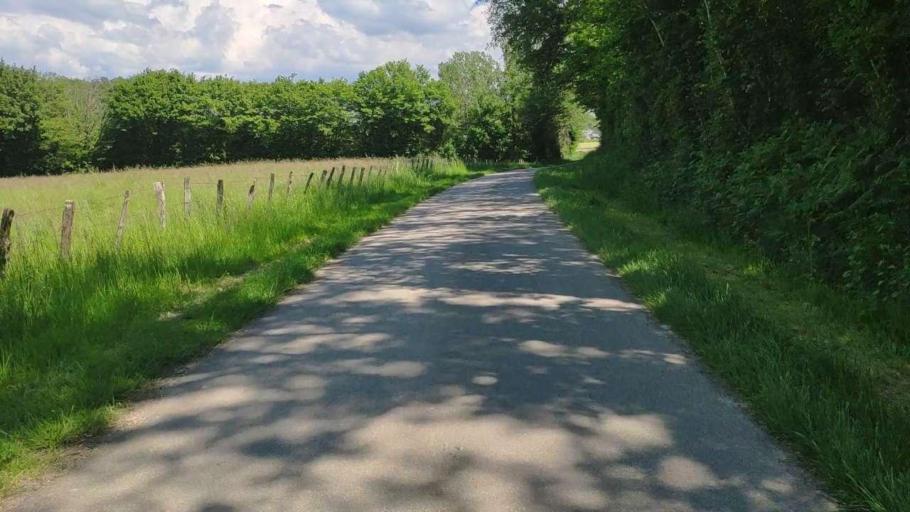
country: FR
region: Franche-Comte
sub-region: Departement du Jura
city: Bletterans
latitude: 46.7879
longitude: 5.4105
